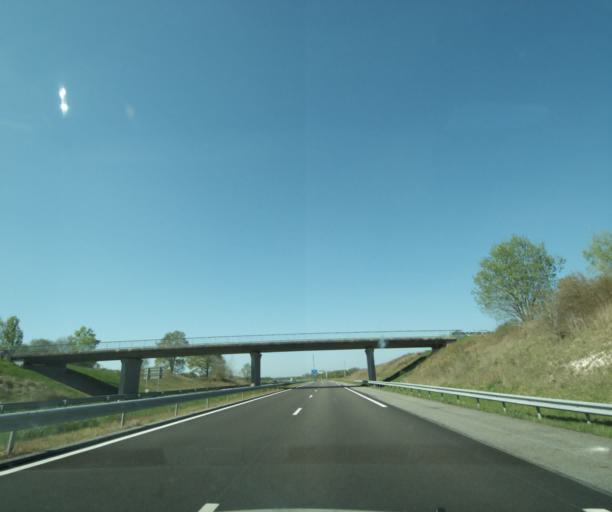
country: FR
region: Centre
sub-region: Departement du Loiret
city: Bonny-sur-Loire
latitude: 47.5649
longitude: 2.8802
